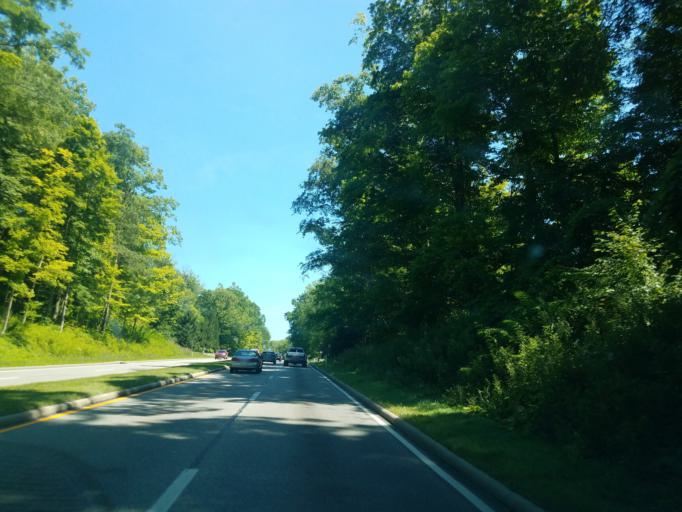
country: US
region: Ohio
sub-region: Cuyahoga County
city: Gates Mills
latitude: 41.5264
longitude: -81.4009
